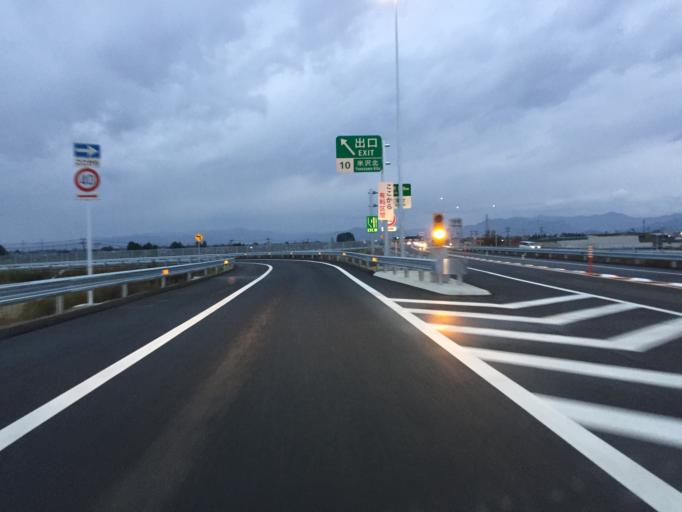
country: JP
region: Yamagata
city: Yonezawa
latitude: 37.9539
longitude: 140.1156
